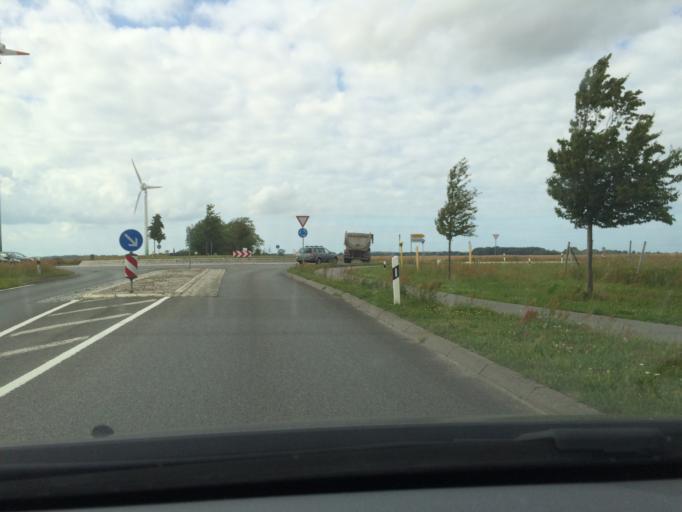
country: DE
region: Mecklenburg-Vorpommern
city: Kramerhof
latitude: 54.3510
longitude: 13.0434
